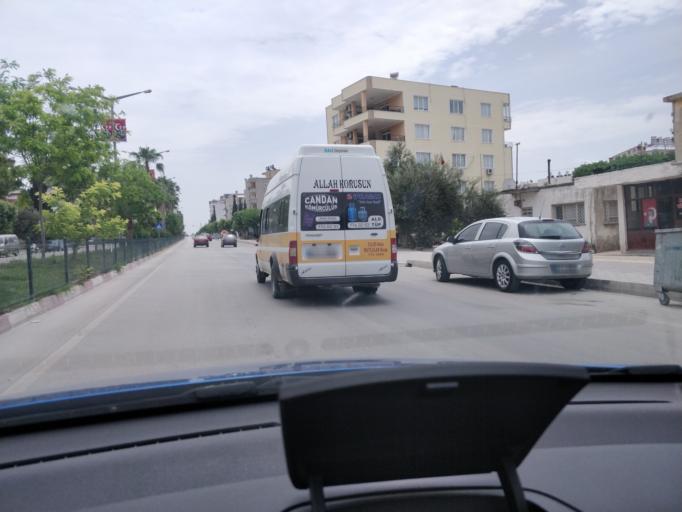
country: TR
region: Mersin
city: Mut
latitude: 36.6405
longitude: 33.4420
